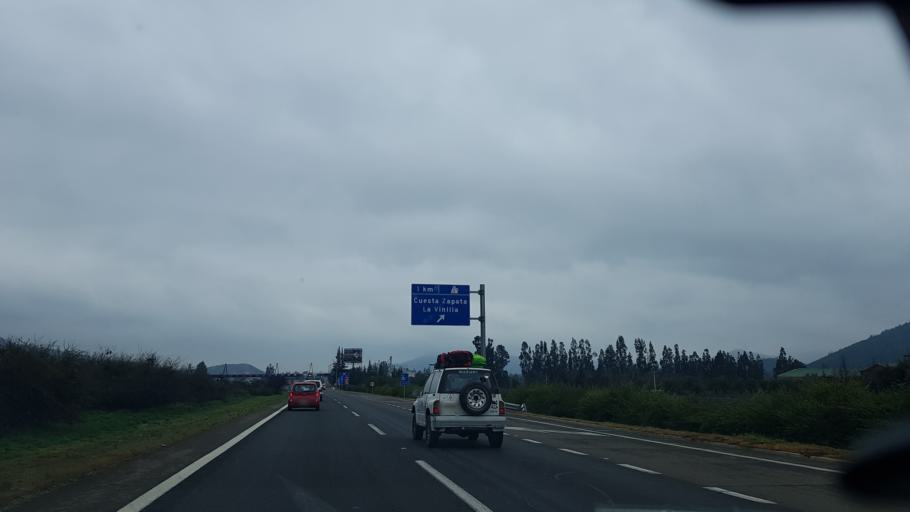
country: CL
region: Santiago Metropolitan
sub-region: Provincia de Melipilla
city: Melipilla
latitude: -33.3736
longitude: -71.2932
